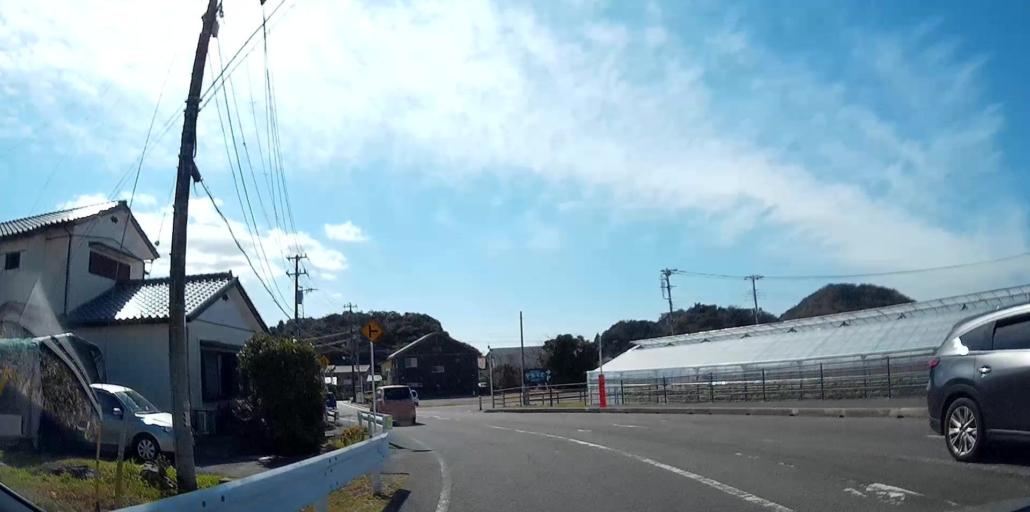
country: JP
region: Chiba
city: Tateyama
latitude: 35.0373
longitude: 139.8506
